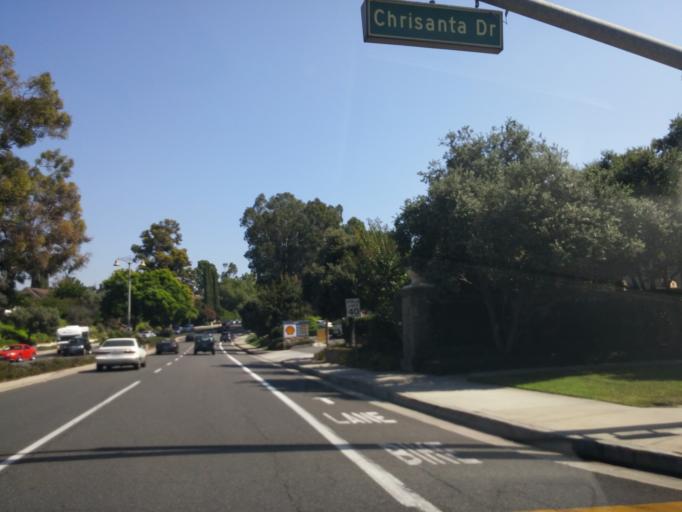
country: US
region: California
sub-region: Orange County
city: Mission Viejo
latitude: 33.6004
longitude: -117.6720
